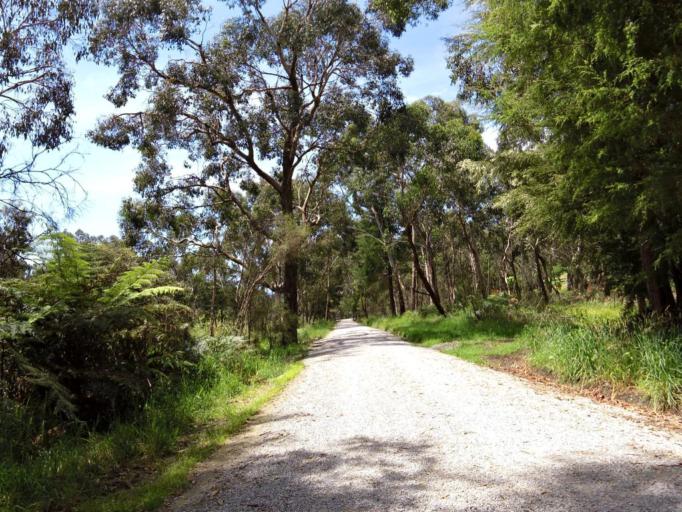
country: AU
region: Victoria
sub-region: Yarra Ranges
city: Mount Evelyn
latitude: -37.7776
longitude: 145.4327
